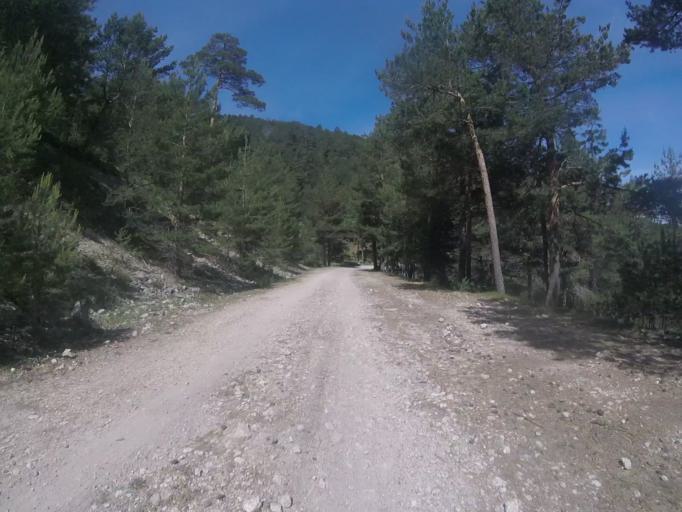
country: ES
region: Madrid
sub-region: Provincia de Madrid
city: Cercedilla
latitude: 40.8073
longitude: -4.0544
